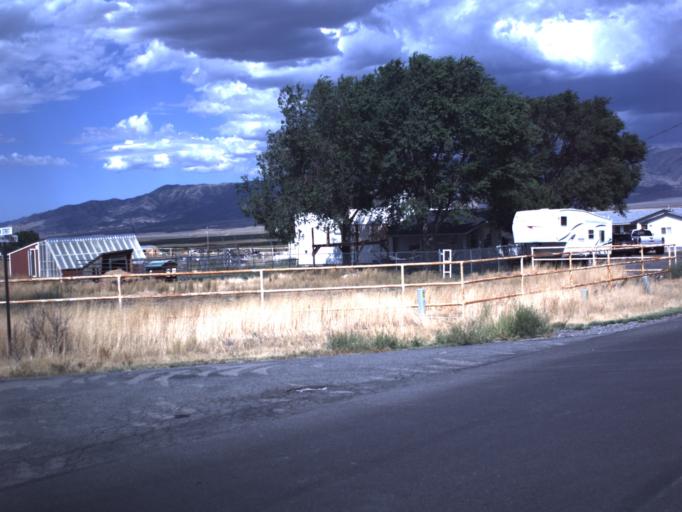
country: US
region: Utah
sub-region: Tooele County
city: Tooele
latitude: 40.3366
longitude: -112.4458
